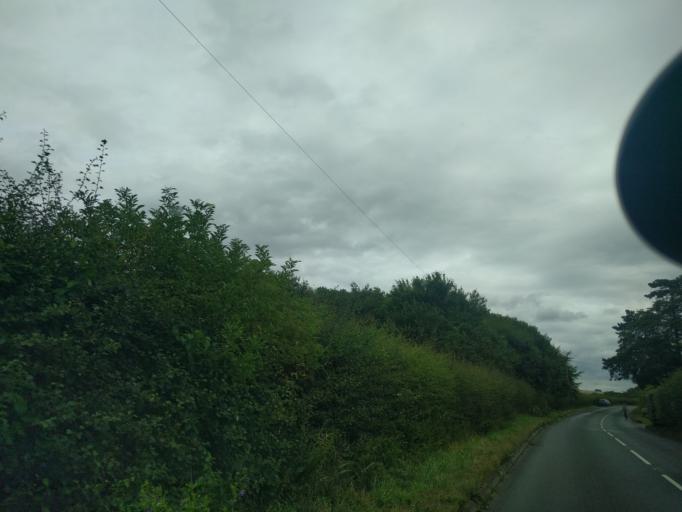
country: GB
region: England
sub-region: Wiltshire
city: Erlestoke
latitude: 51.2802
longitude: -2.0235
